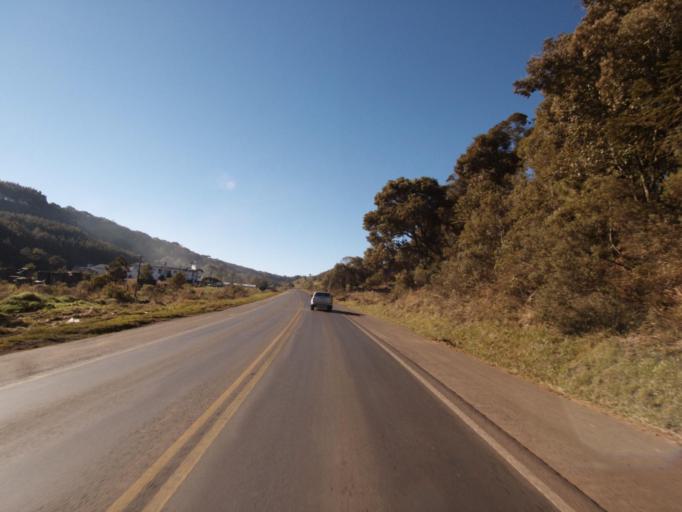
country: BR
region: Santa Catarina
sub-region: Concordia
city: Concordia
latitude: -26.8843
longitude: -52.0102
